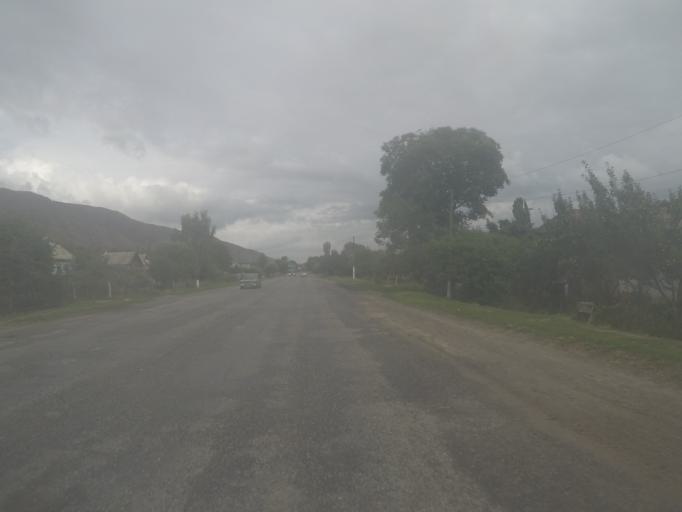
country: KG
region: Ysyk-Koel
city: Tyup
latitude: 42.7419
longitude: 78.0185
